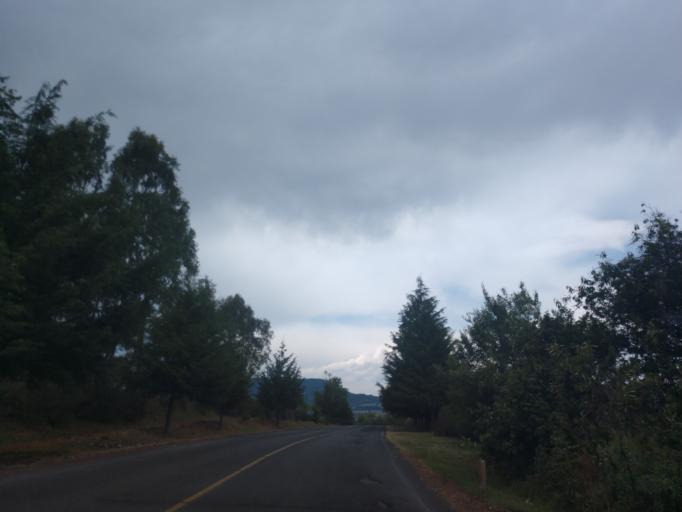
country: MX
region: Jalisco
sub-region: Mazamitla
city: Mazamitla
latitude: 19.9221
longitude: -103.0389
